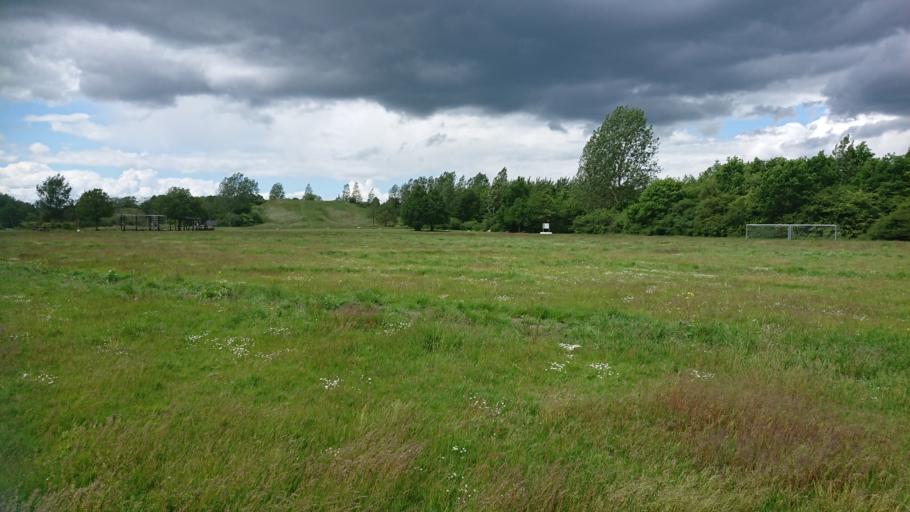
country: DK
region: Capital Region
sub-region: Ballerup Kommune
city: Ballerup
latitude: 55.7109
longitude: 12.3626
